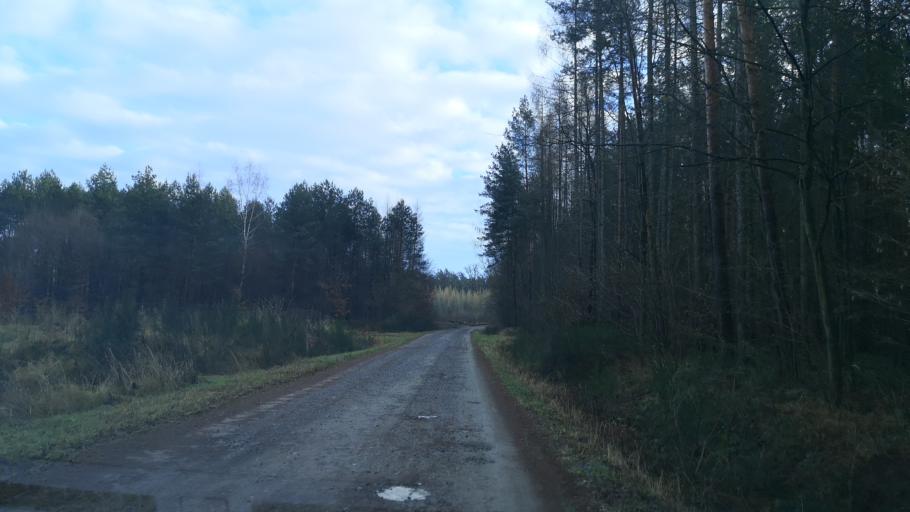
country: PL
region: Subcarpathian Voivodeship
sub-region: Powiat lezajski
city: Piskorowice
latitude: 50.2523
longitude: 22.5671
